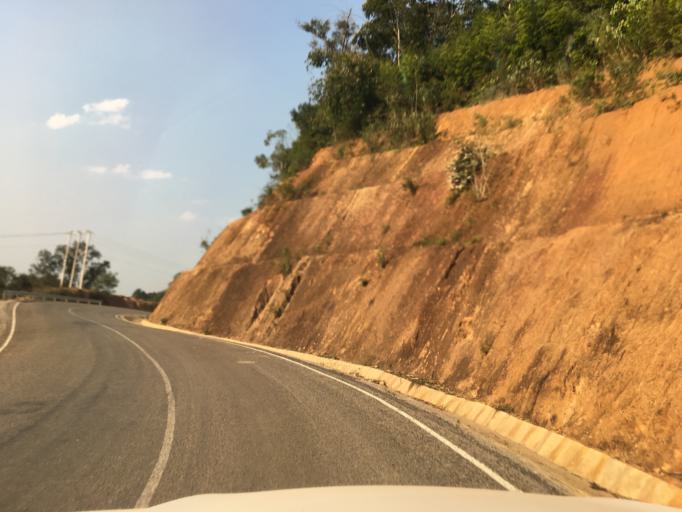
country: LA
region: Houaphan
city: Xam Nua
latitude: 20.5852
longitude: 104.0579
